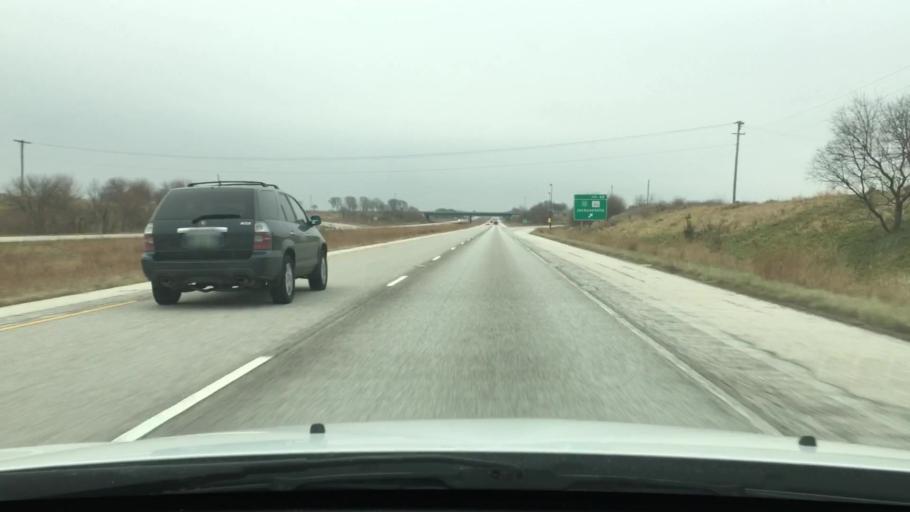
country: US
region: Illinois
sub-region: Morgan County
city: South Jacksonville
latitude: 39.7183
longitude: -90.1724
